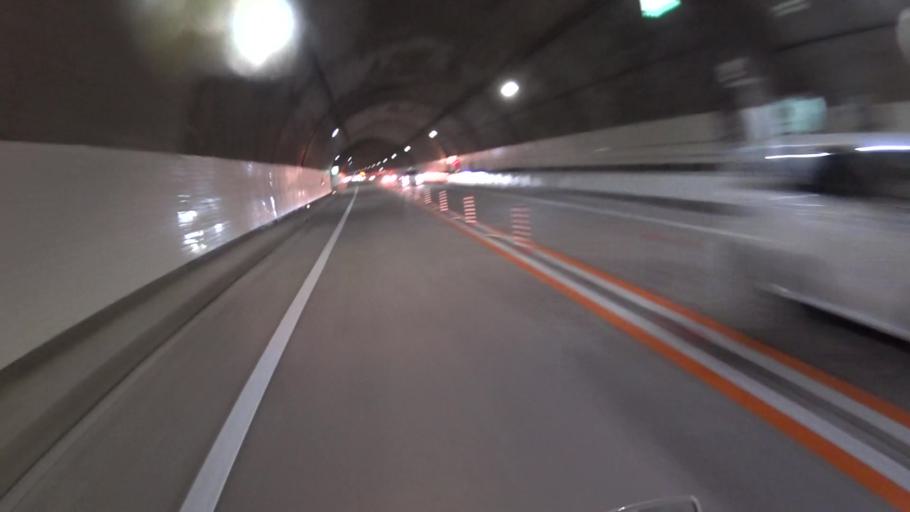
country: JP
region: Kyoto
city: Ayabe
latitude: 35.2316
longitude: 135.3453
